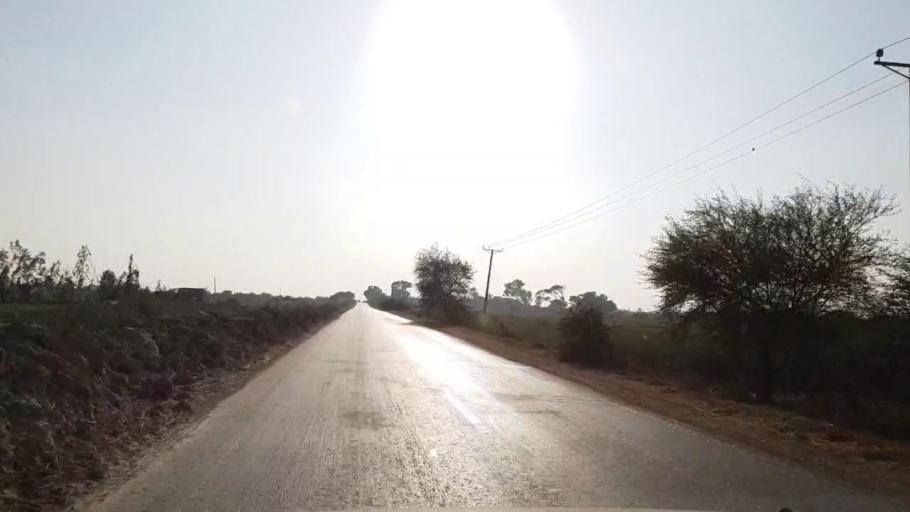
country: PK
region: Sindh
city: Mirpur Batoro
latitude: 24.7899
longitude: 68.2968
